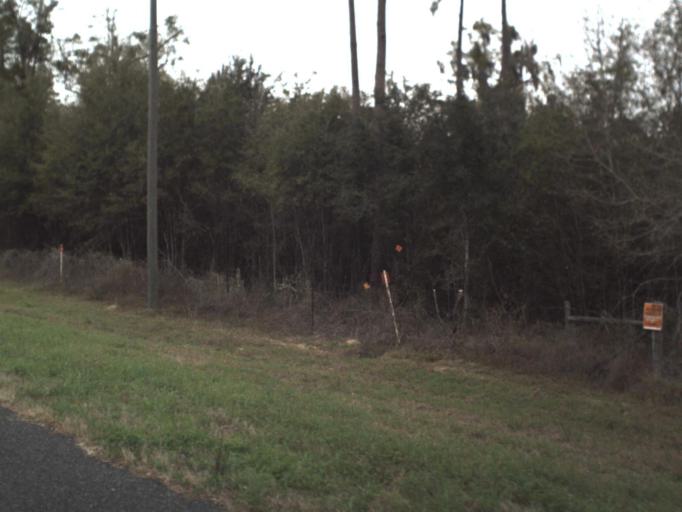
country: US
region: Florida
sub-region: Jefferson County
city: Monticello
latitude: 30.4091
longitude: -83.9712
